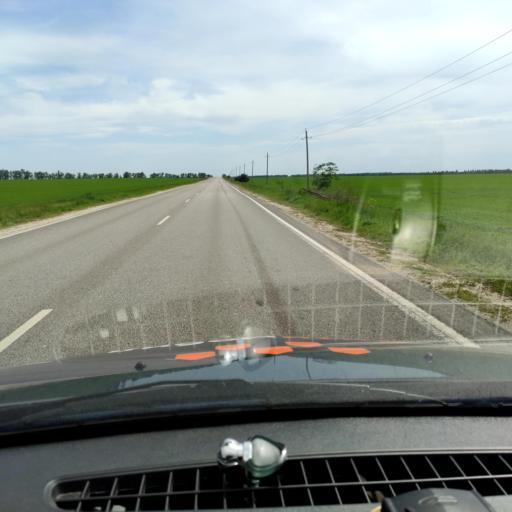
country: RU
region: Voronezj
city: Novaya Usman'
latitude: 51.5639
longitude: 39.3759
